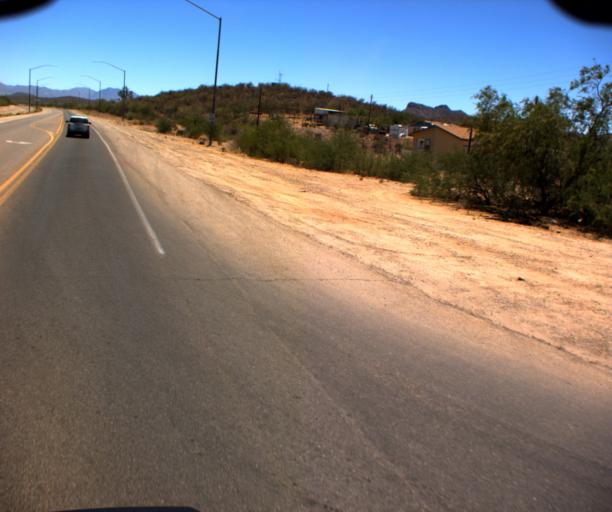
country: US
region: Arizona
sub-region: Pima County
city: Sells
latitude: 31.9185
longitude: -111.8799
